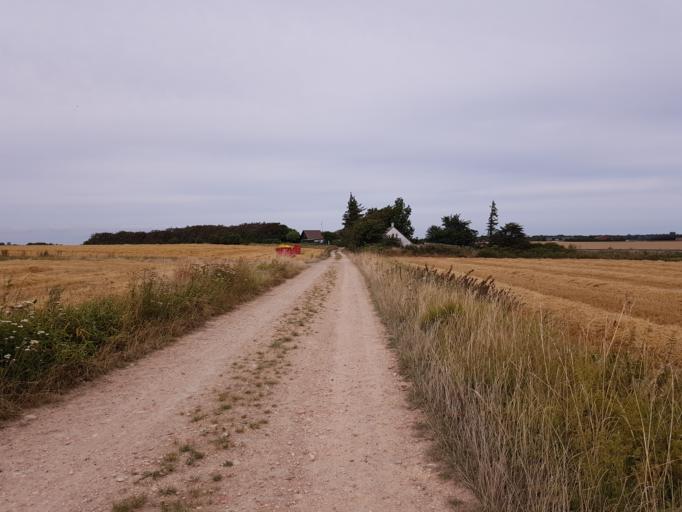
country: DK
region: Zealand
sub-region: Guldborgsund Kommune
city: Nykobing Falster
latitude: 54.5939
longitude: 11.9259
